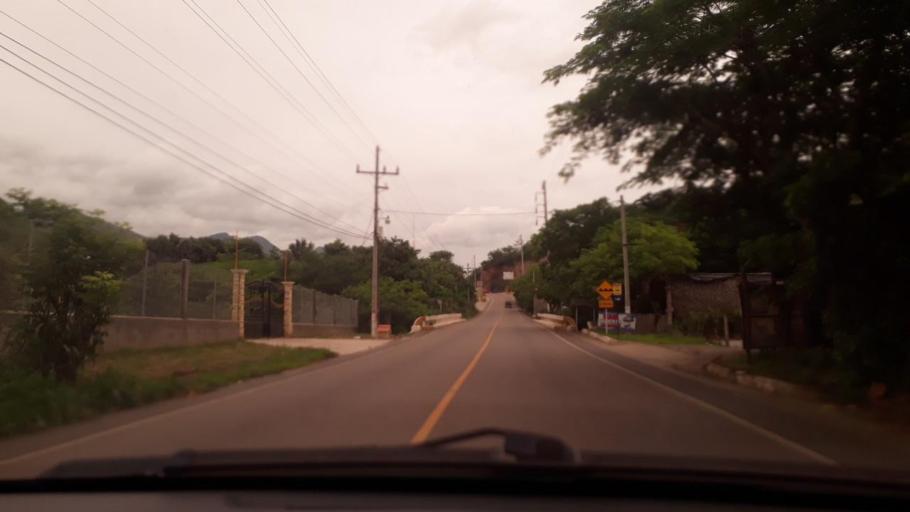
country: GT
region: Chiquimula
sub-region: Municipio de Jocotan
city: Jocotan
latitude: 14.8141
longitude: -89.3845
